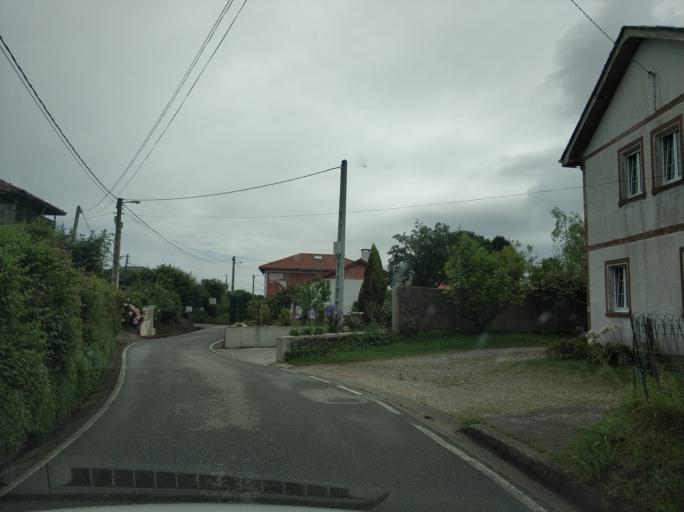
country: ES
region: Asturias
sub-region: Province of Asturias
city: Salas
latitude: 43.5492
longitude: -6.3843
